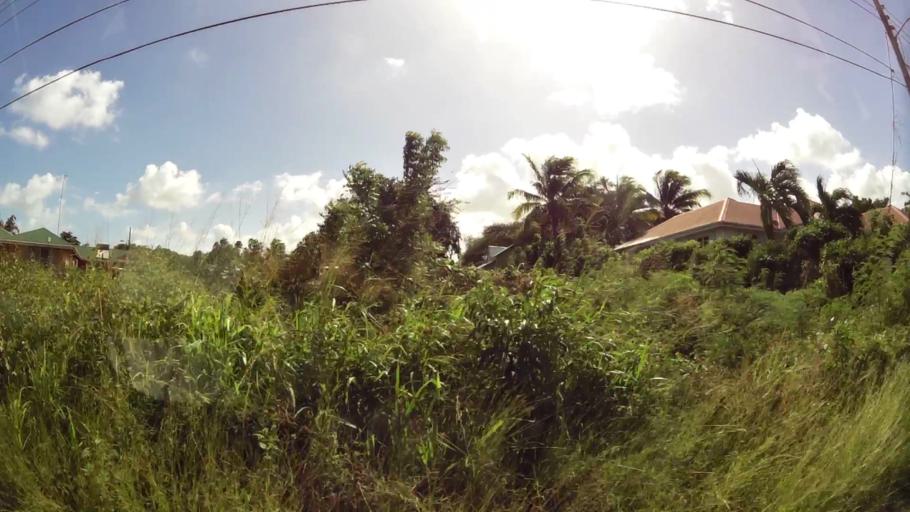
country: AG
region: Saint George
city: Piggotts
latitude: 17.1681
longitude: -61.8030
